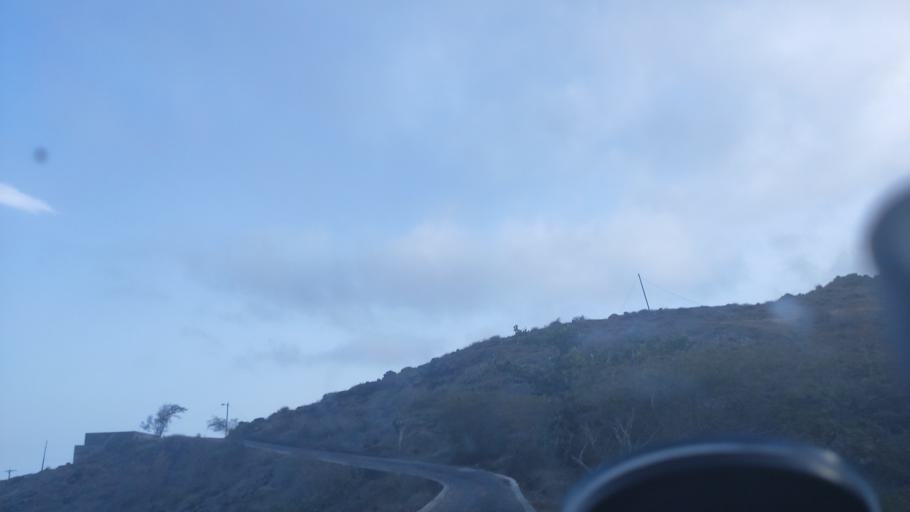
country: CV
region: Mosteiros
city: Porto dos Mosteiros
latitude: 15.0066
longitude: -24.3050
